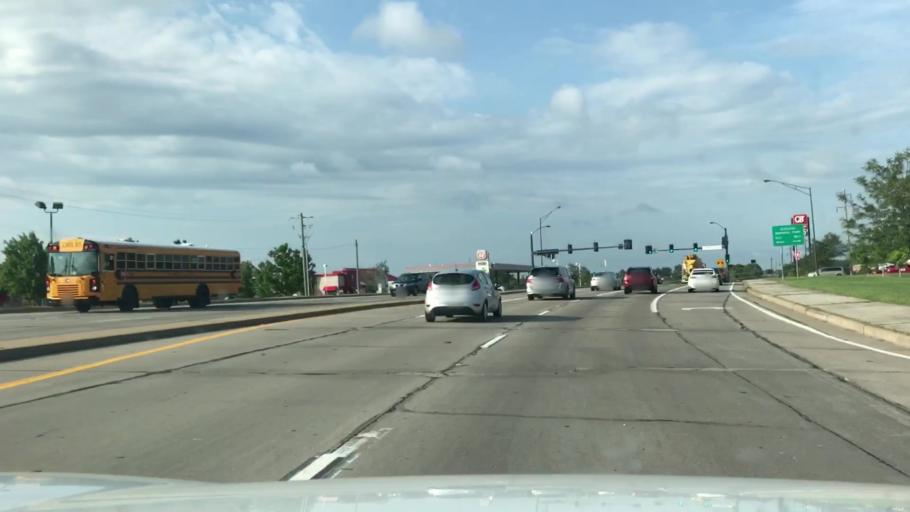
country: US
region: Missouri
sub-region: Saint Charles County
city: Dardenne Prairie
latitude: 38.8013
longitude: -90.7335
